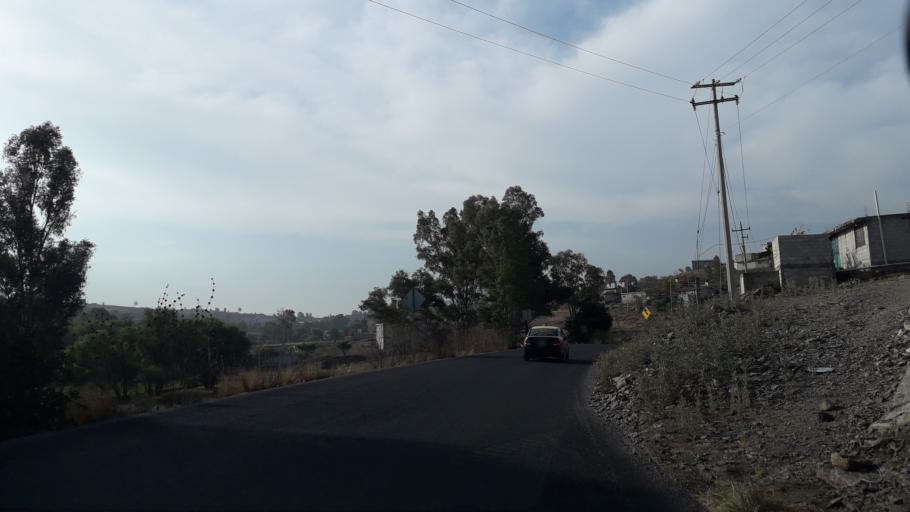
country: MX
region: Puebla
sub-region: Puebla
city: San Andres Azumiatla
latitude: 18.9251
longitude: -98.2530
